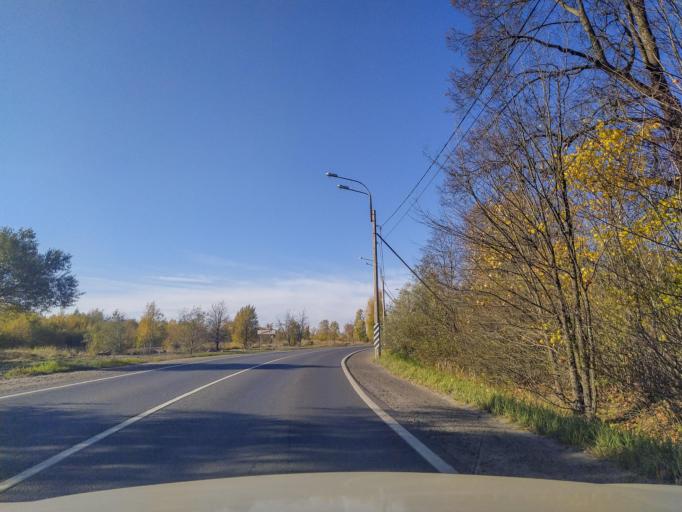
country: RU
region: St.-Petersburg
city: Aleksandrovskaya
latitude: 59.7036
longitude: 30.3504
